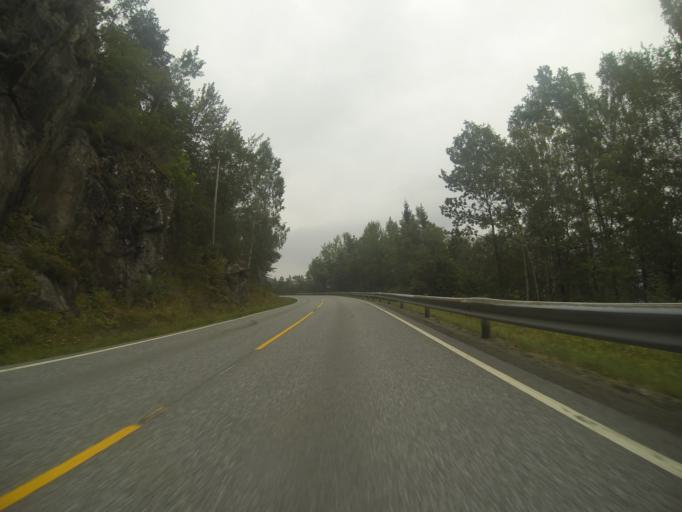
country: NO
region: Rogaland
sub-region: Suldal
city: Sand
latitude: 59.5145
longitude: 6.2277
